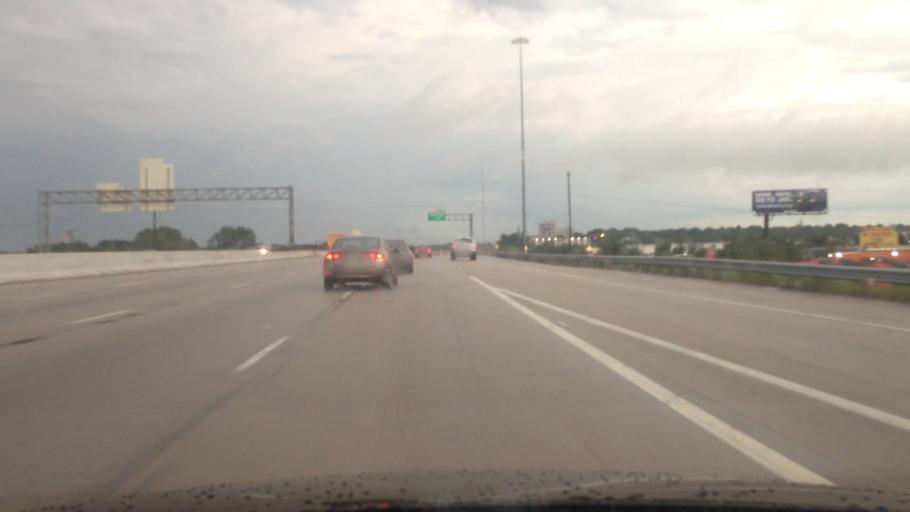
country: US
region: Texas
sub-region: Tarrant County
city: Fort Worth
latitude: 32.7483
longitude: -97.3050
